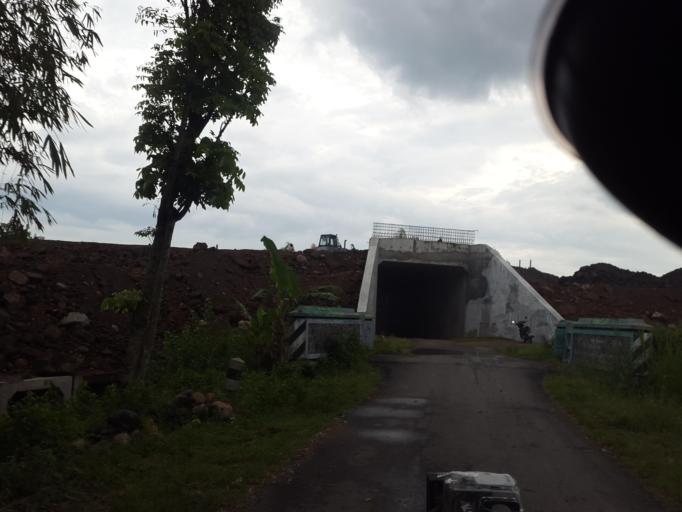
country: ID
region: East Java
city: Madiun
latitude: -7.5224
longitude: 111.6502
